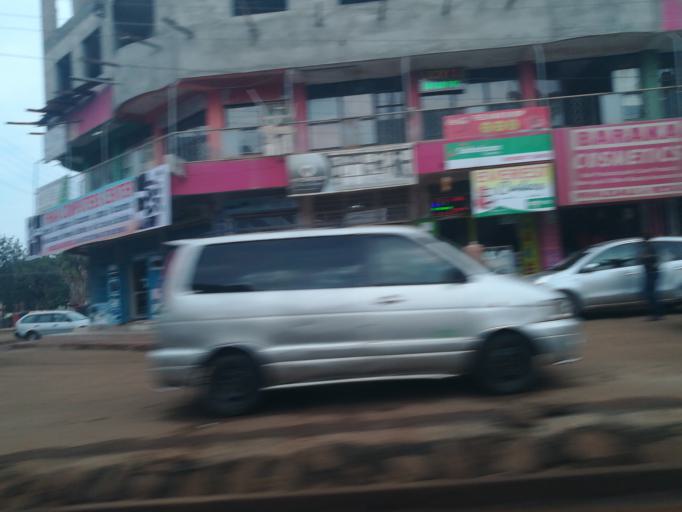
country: KE
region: Nairobi Area
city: Thika
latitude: -1.0397
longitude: 37.0720
